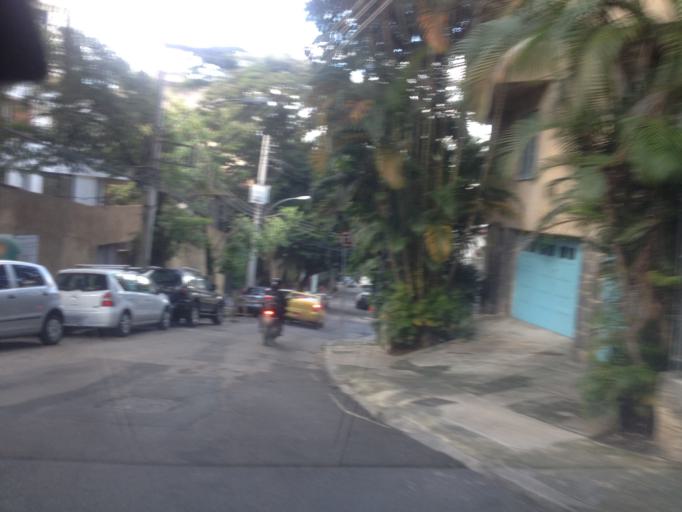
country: BR
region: Rio de Janeiro
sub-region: Rio De Janeiro
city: Rio de Janeiro
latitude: -22.9583
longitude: -43.2075
